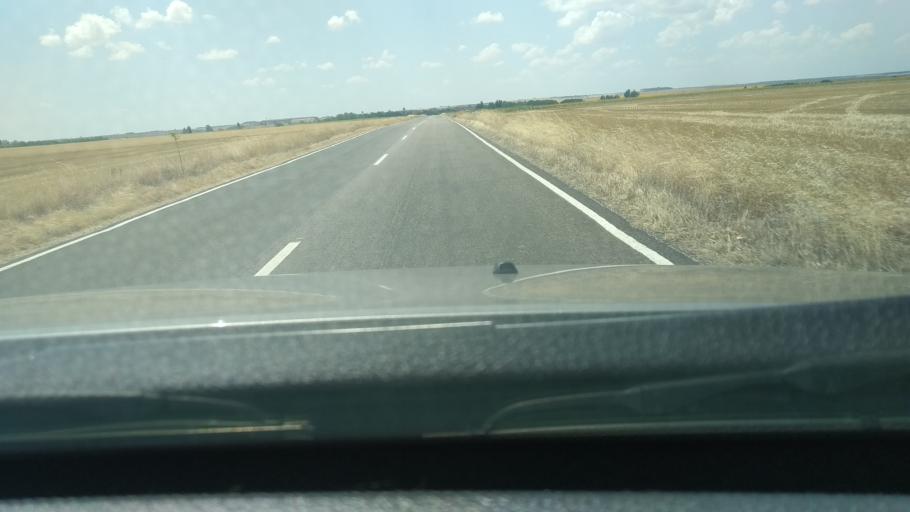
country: ES
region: Castille and Leon
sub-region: Provincia de Burgos
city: Villafruela
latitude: 41.9250
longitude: -3.8979
